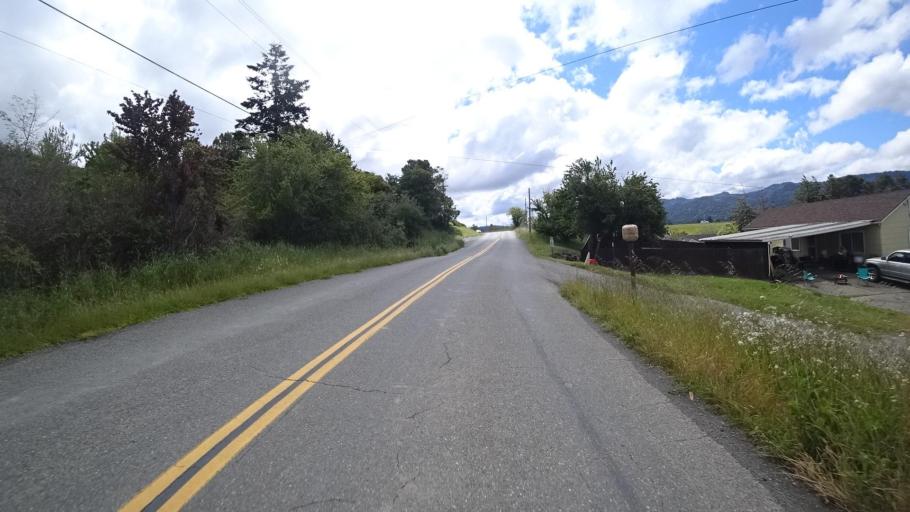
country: US
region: California
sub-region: Humboldt County
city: Blue Lake
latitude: 40.8905
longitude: -123.9996
